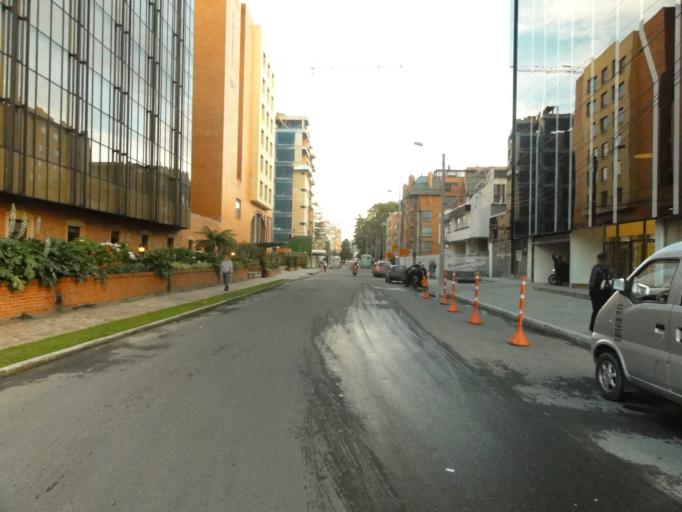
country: CO
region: Bogota D.C.
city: Barrio San Luis
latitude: 4.6861
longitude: -74.0546
